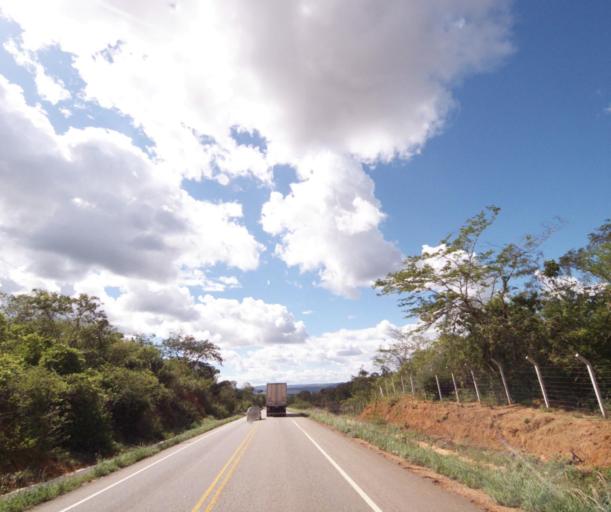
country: BR
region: Bahia
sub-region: Caetite
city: Caetite
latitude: -14.1357
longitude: -42.3859
